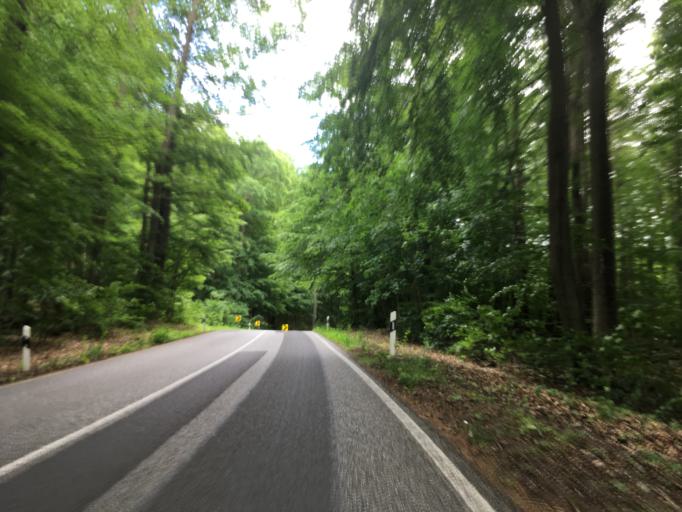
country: DE
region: Brandenburg
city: Bad Freienwalde
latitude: 52.7438
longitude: 13.9888
